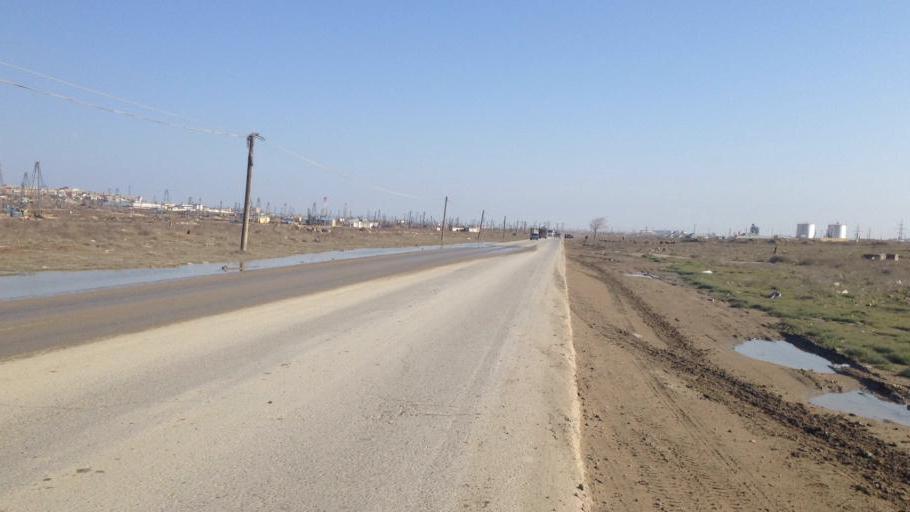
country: AZ
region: Baki
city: Balakhani
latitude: 40.4526
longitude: 49.8974
